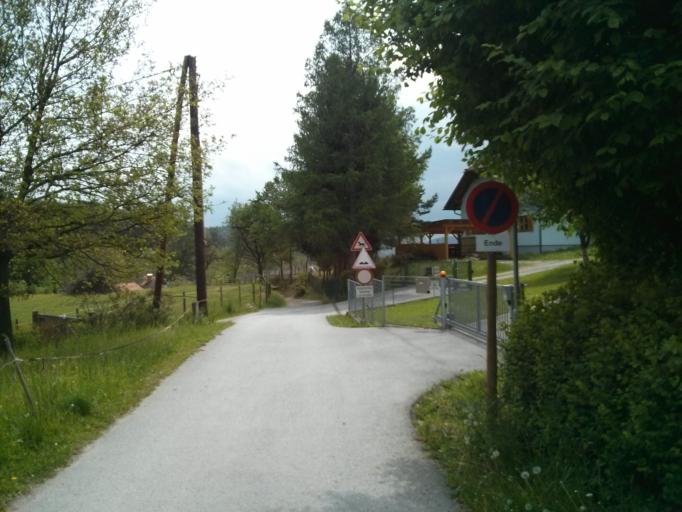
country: AT
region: Styria
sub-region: Politischer Bezirk Graz-Umgebung
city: Stattegg
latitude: 47.1358
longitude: 15.4236
